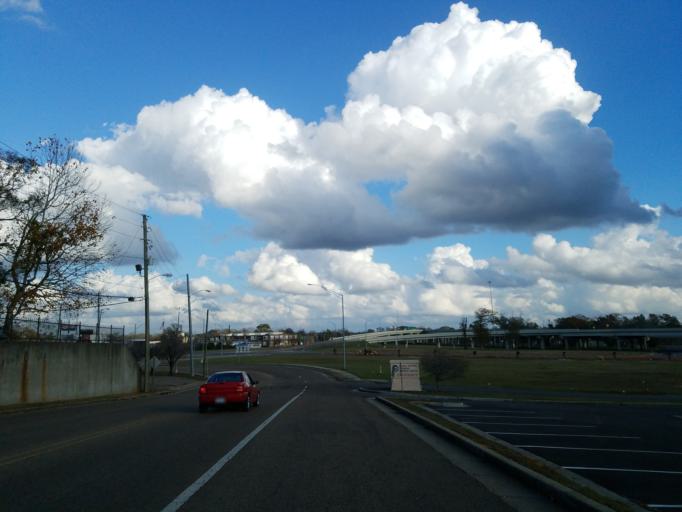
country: US
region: Mississippi
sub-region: Jones County
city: Laurel
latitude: 31.6858
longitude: -89.1399
